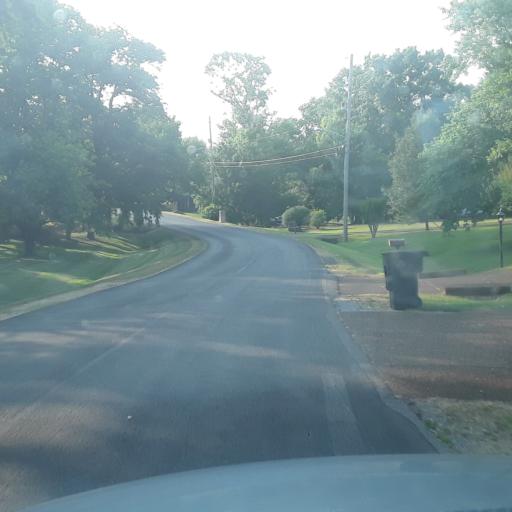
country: US
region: Tennessee
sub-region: Williamson County
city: Brentwood Estates
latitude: 36.0347
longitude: -86.7383
